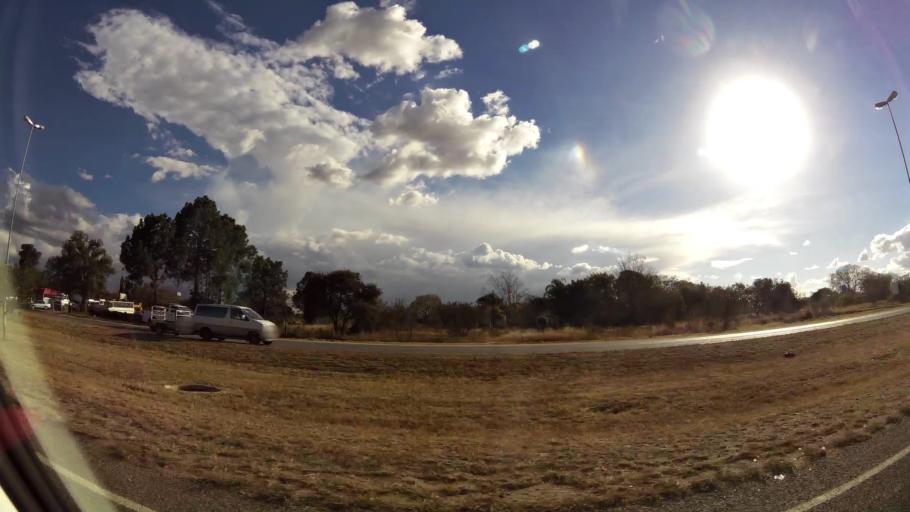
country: ZA
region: Limpopo
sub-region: Capricorn District Municipality
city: Polokwane
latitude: -23.9383
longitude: 29.4491
